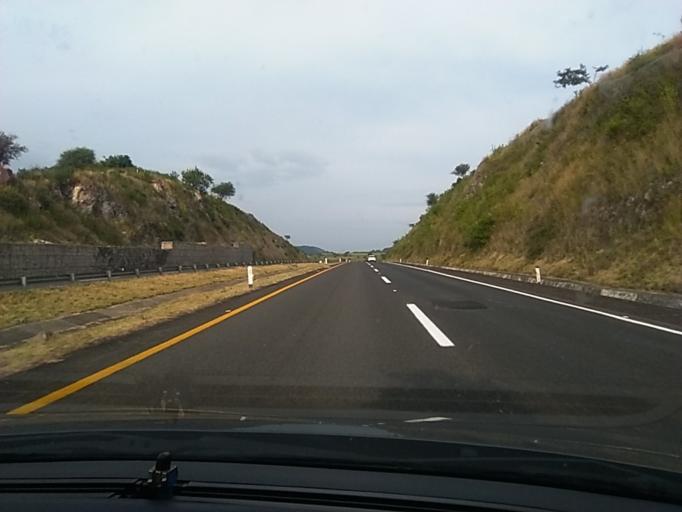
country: MX
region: Michoacan
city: Copandaro de Galeana
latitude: 19.8894
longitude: -101.1775
